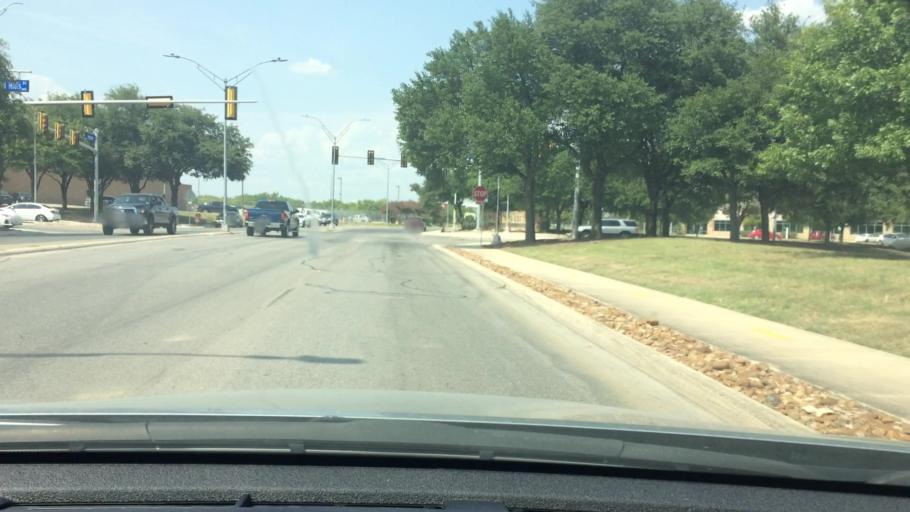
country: US
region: Texas
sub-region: Bexar County
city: Leon Valley
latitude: 29.4417
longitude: -98.6569
